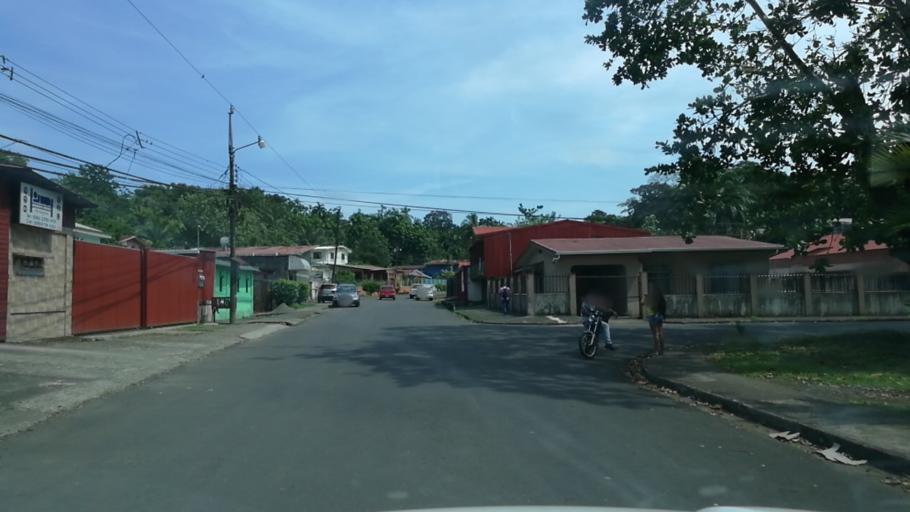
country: CR
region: Limon
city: Limon
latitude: 10.0072
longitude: -83.0579
